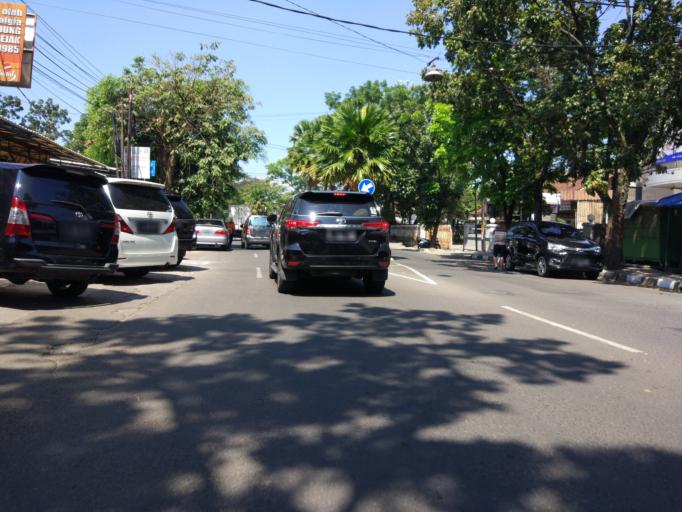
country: ID
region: West Java
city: Bandung
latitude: -6.9274
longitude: 107.6195
